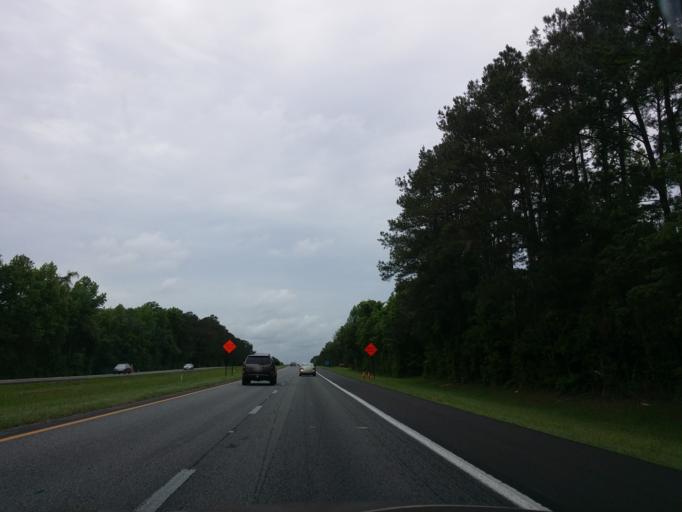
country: US
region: Florida
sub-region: Jefferson County
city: Monticello
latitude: 30.4452
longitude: -83.7056
